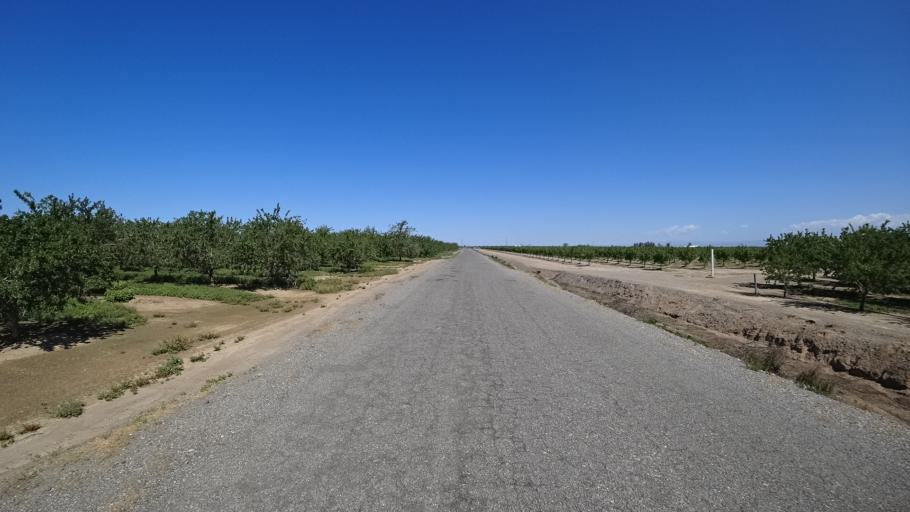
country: US
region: California
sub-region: Glenn County
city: Orland
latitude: 39.6855
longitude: -122.1221
